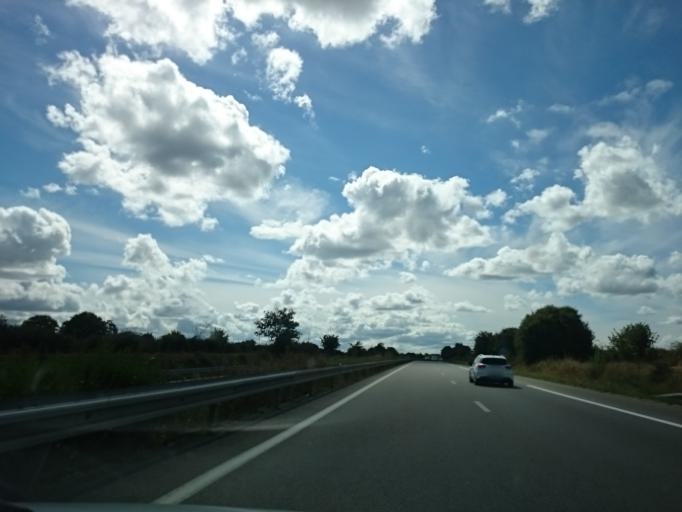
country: FR
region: Pays de la Loire
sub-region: Departement de la Loire-Atlantique
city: Oudon
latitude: 47.3609
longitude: -1.3201
